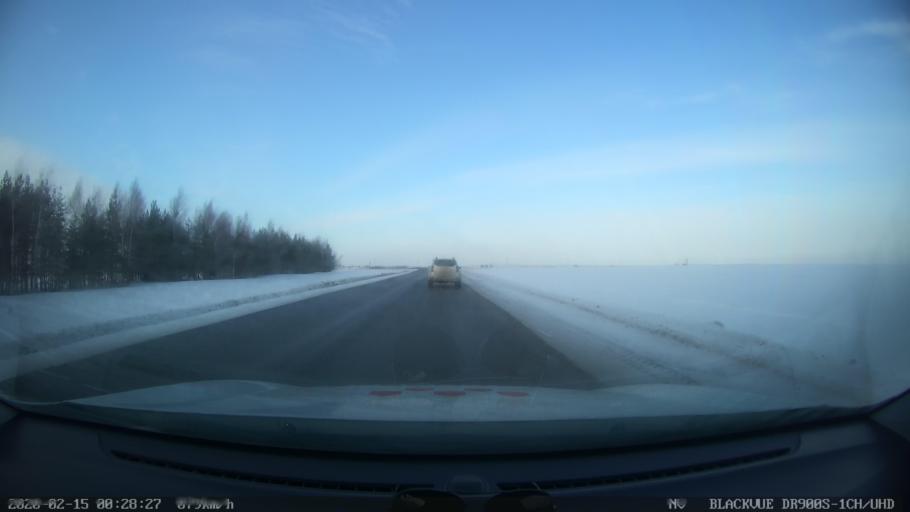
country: RU
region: Tatarstan
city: Verkhniy Uslon
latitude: 55.6424
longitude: 48.8764
